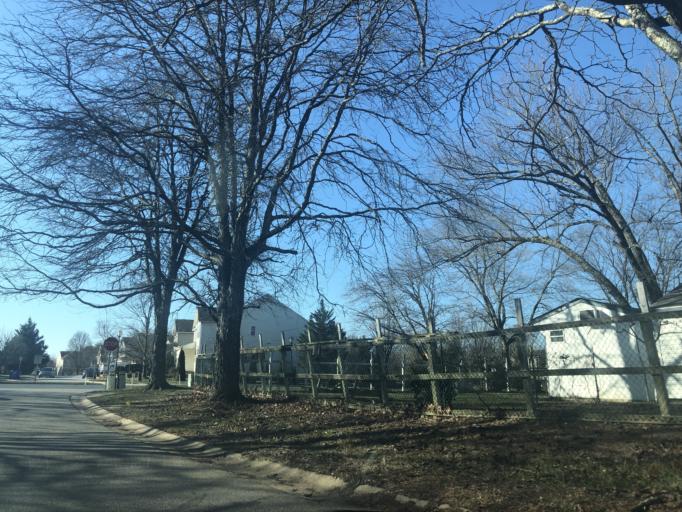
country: US
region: Maryland
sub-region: Howard County
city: Columbia
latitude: 39.2077
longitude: -76.8303
